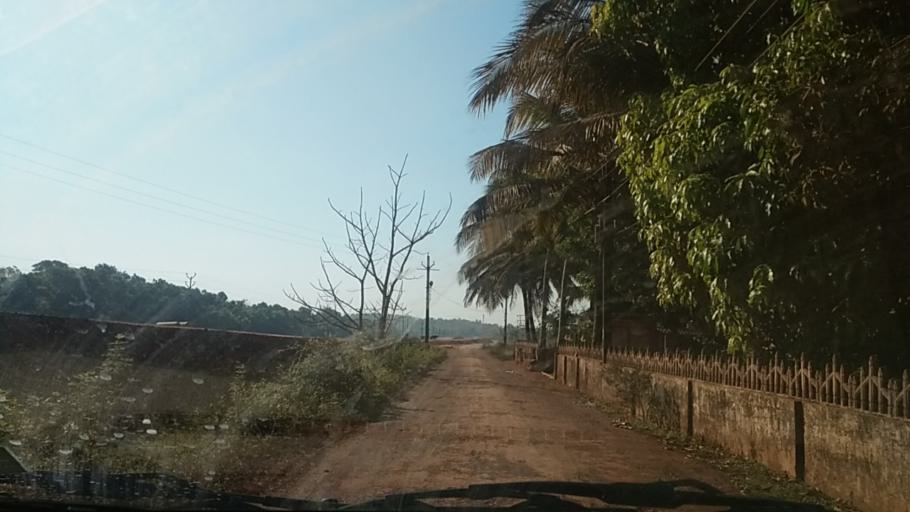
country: IN
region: Karnataka
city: Canacona
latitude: 15.0085
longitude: 74.0375
